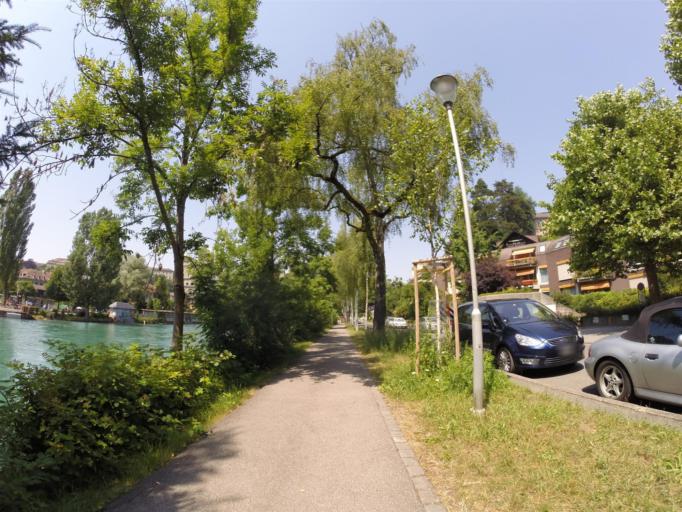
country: CH
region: Bern
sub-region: Bern-Mittelland District
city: Bern
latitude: 46.9429
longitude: 7.4457
